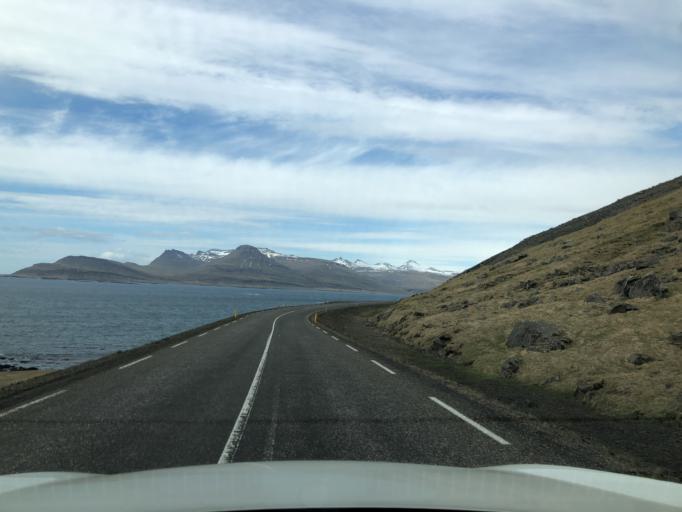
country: IS
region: East
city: Eskifjoerdur
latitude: 64.7965
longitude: -13.9067
